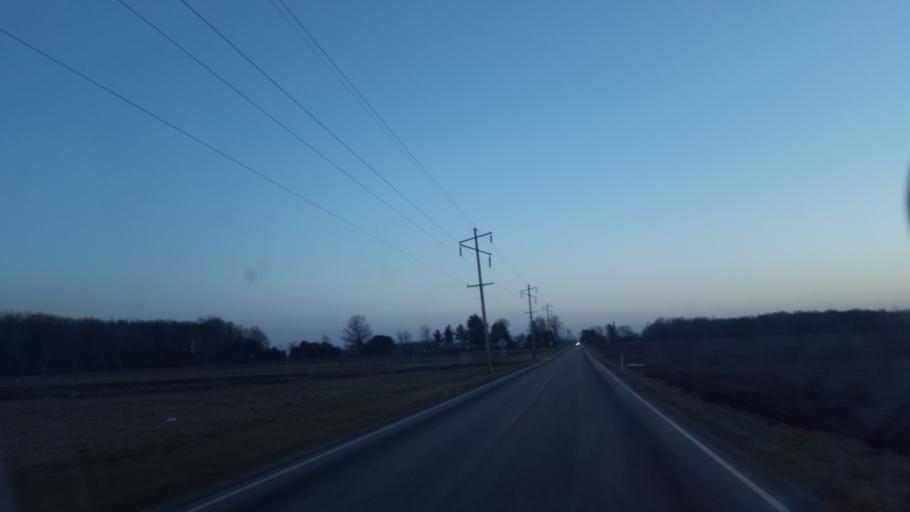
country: US
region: Indiana
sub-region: Elkhart County
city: Nappanee
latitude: 41.3967
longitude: -86.0010
